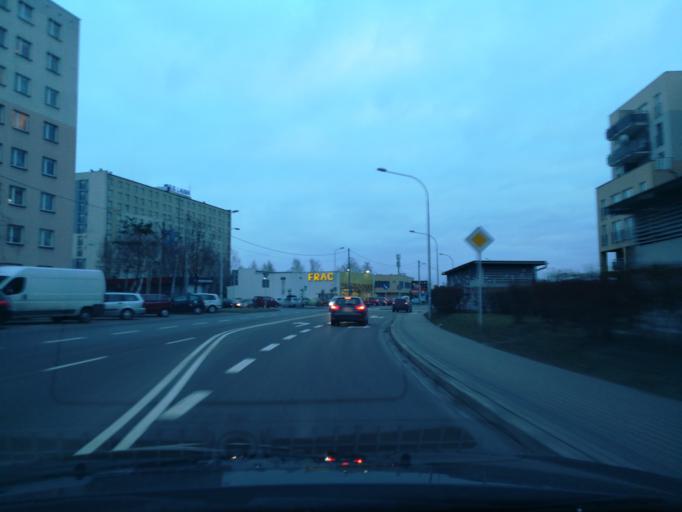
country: PL
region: Subcarpathian Voivodeship
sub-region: Rzeszow
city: Rzeszow
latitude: 50.0184
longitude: 22.0040
